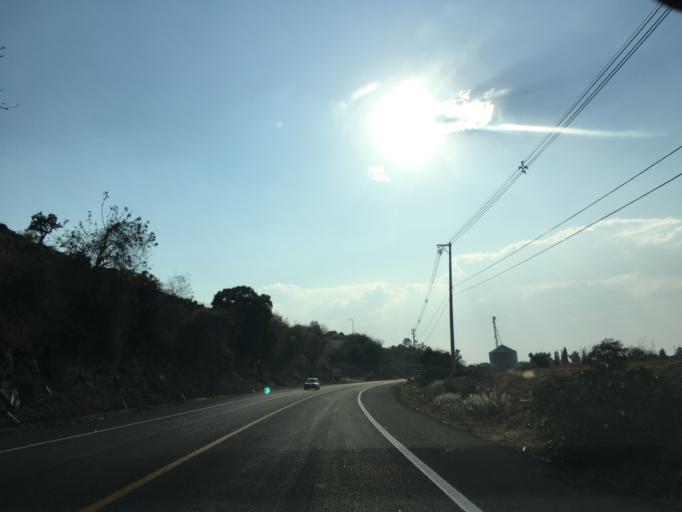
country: MX
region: Michoacan
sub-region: Indaparapeo
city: Colonia de Guadalupe
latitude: 19.8064
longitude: -100.8754
